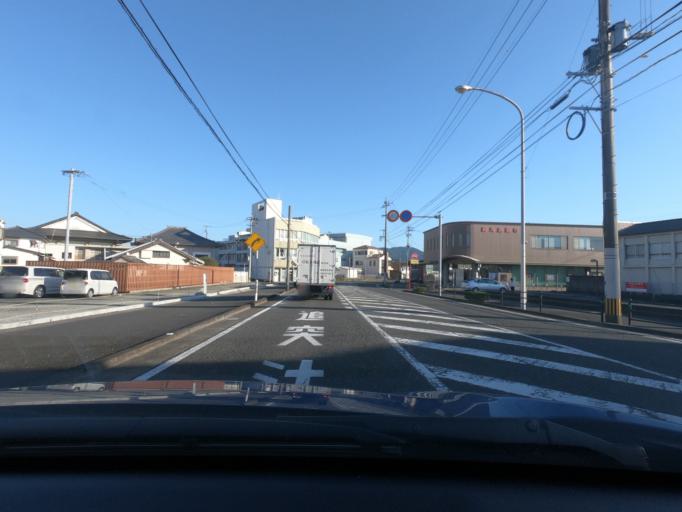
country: JP
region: Kagoshima
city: Akune
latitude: 32.0186
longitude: 130.1965
